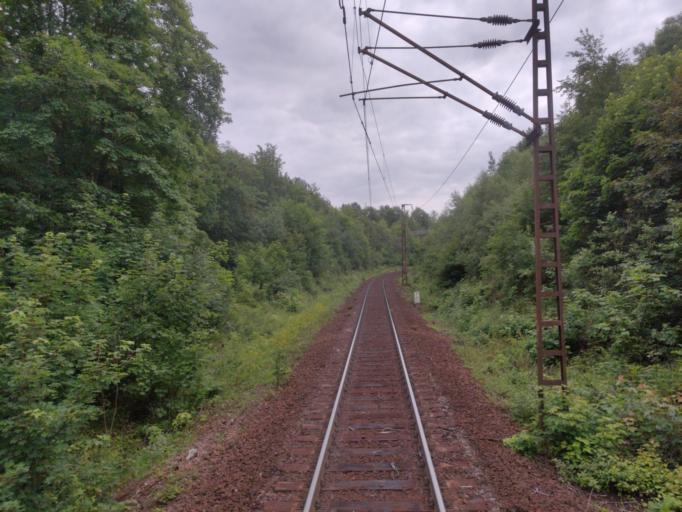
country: DE
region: Saxony-Anhalt
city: Huttenrode
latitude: 51.7866
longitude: 10.9238
